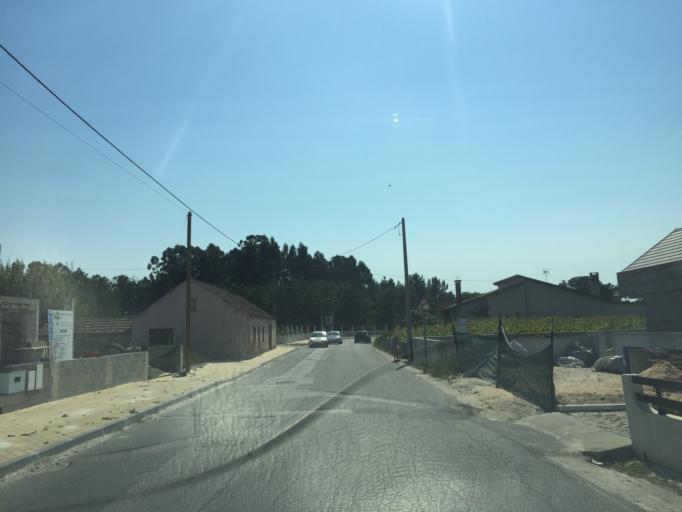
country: PT
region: Coimbra
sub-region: Montemor-O-Velho
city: Arazede
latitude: 40.3193
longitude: -8.7129
